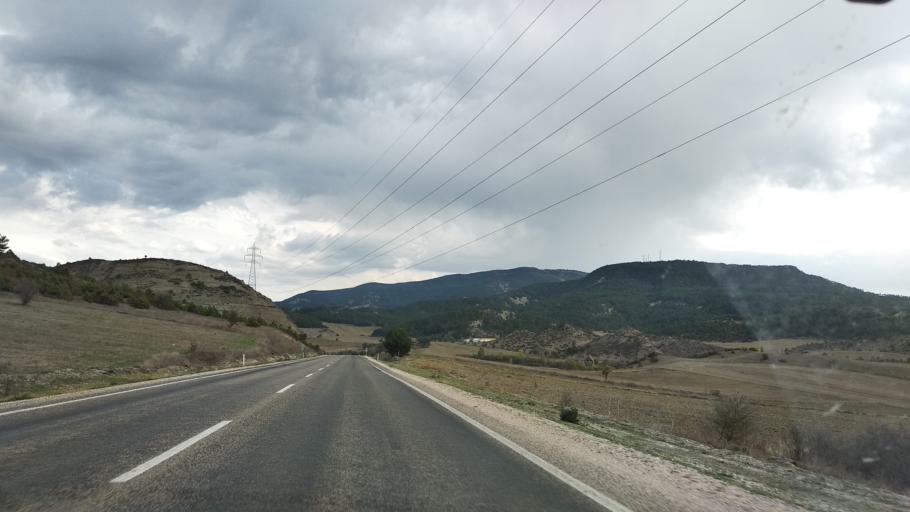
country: TR
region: Bolu
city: Mudurnu
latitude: 40.4785
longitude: 31.1641
